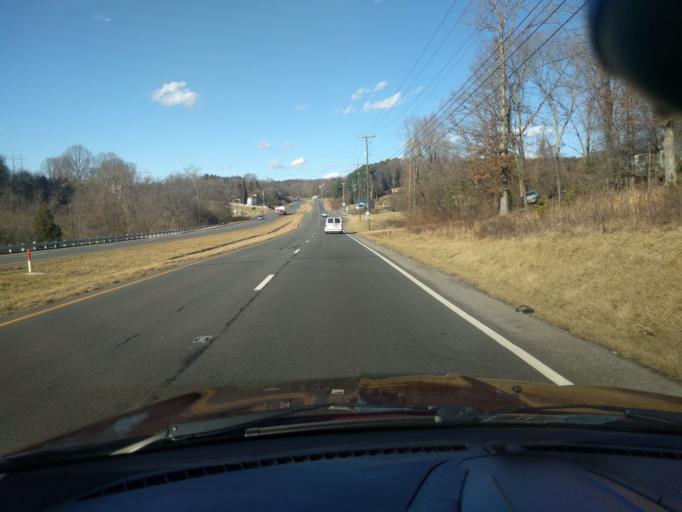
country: US
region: Virginia
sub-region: Botetourt County
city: Cloverdale
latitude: 37.3690
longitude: -79.8864
